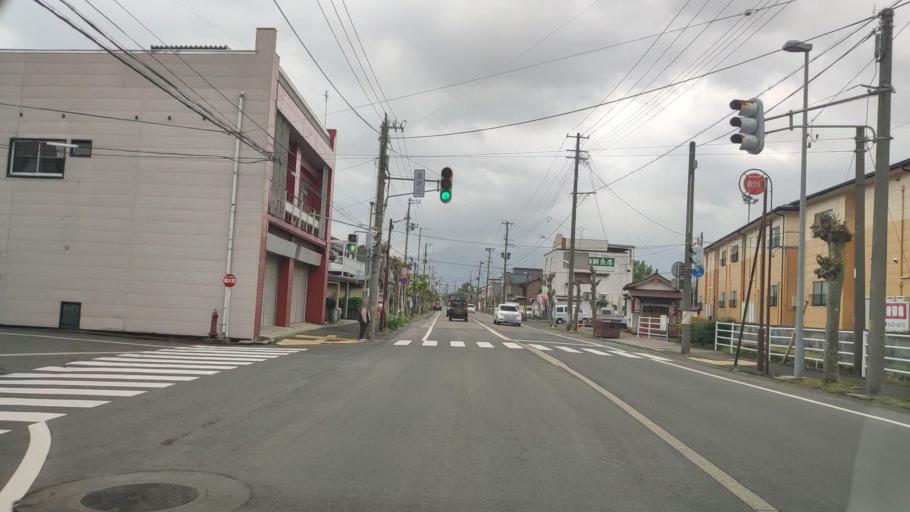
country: JP
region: Niigata
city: Gosen
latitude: 37.7375
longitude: 139.1827
